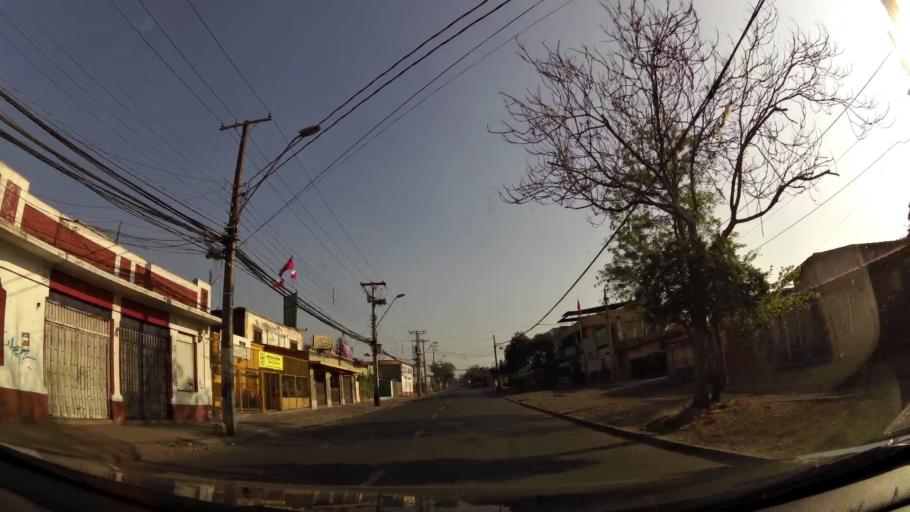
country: CL
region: Santiago Metropolitan
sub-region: Provincia de Santiago
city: Santiago
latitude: -33.4032
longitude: -70.6315
